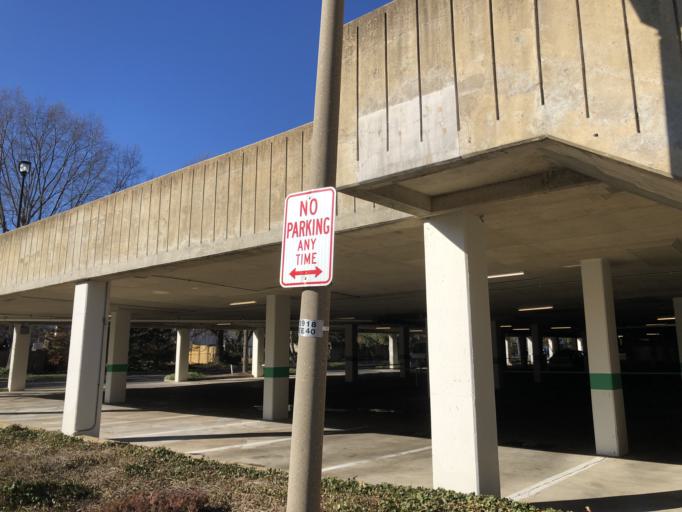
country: US
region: Virginia
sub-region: Arlington County
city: Arlington
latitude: 38.8808
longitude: -77.1173
